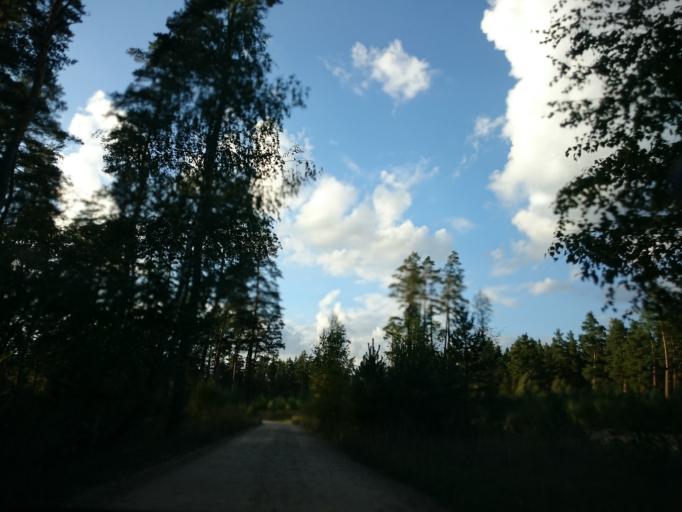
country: LV
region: Adazi
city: Adazi
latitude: 57.0608
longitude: 24.2887
